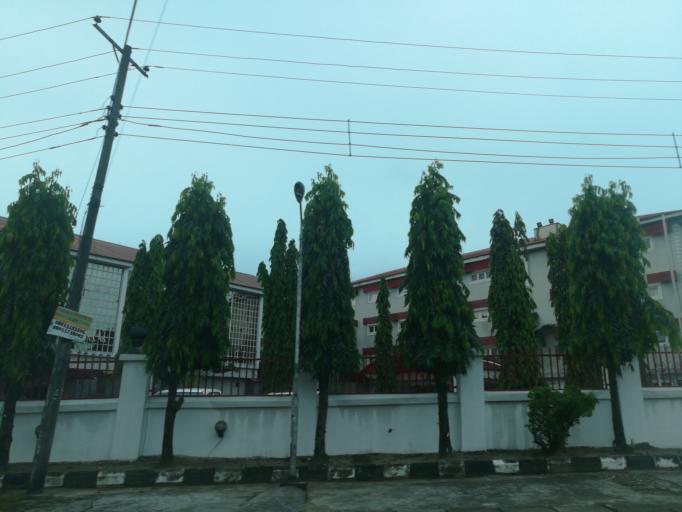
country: NG
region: Rivers
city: Port Harcourt
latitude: 4.8114
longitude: 7.0005
